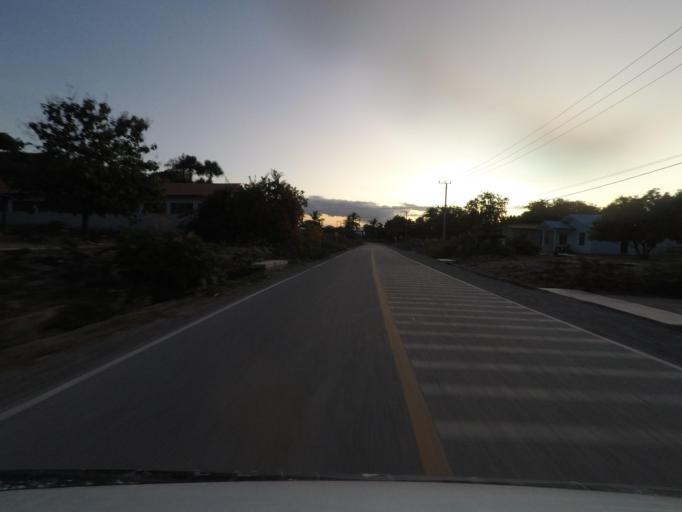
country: TL
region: Baucau
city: Baucau
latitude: -8.4786
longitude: 126.5858
